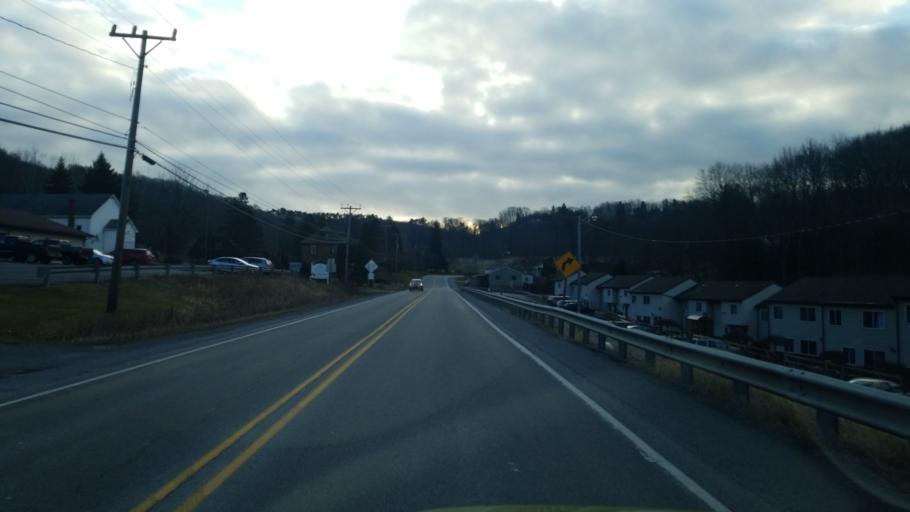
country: US
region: Pennsylvania
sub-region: Clearfield County
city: Clearfield
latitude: 41.0081
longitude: -78.4305
